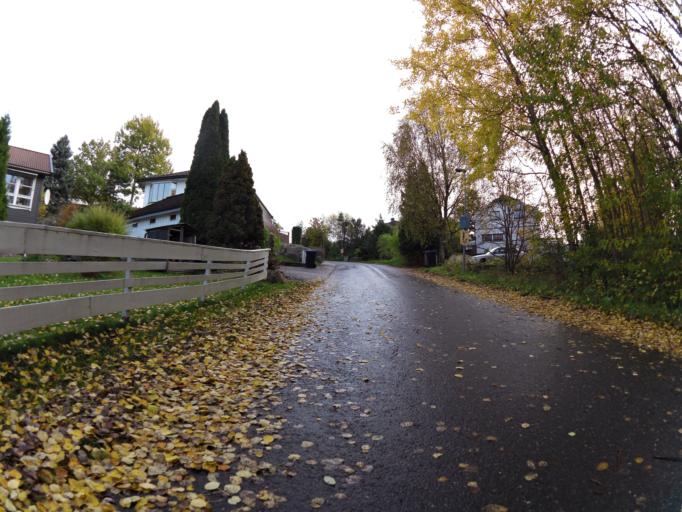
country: NO
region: Ostfold
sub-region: Fredrikstad
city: Fredrikstad
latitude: 59.2246
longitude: 10.9186
